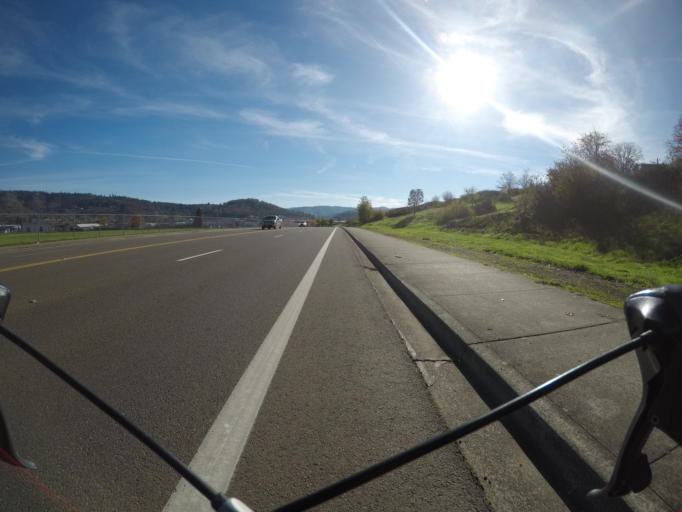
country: US
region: Oregon
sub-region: Douglas County
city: Roseburg
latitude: 43.2322
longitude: -123.3574
